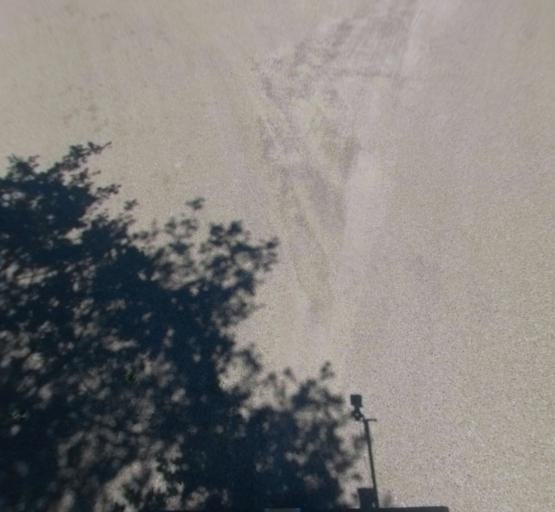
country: US
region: California
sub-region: Fresno County
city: Auberry
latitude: 37.2035
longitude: -119.5588
